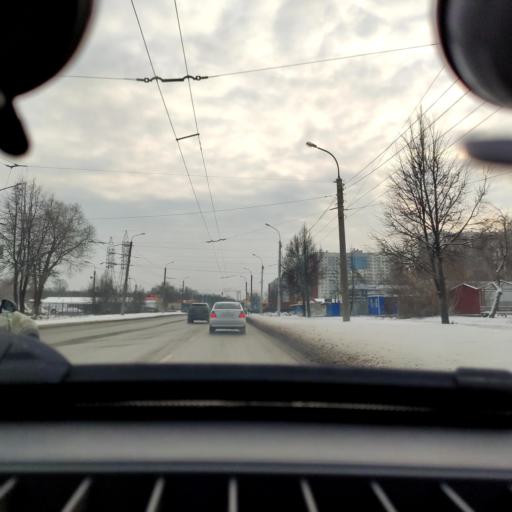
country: RU
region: Bashkortostan
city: Ufa
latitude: 54.7902
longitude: 56.1384
